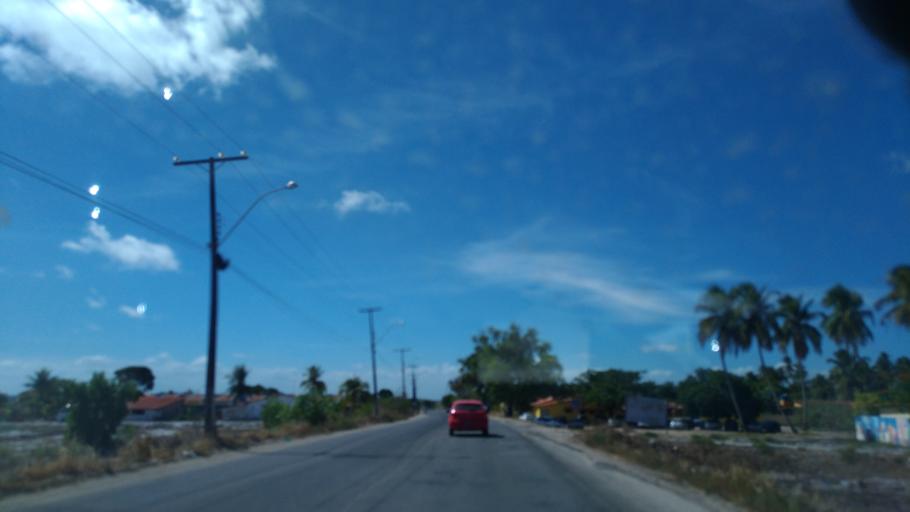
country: BR
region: Alagoas
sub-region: Marechal Deodoro
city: Marechal Deodoro
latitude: -9.7511
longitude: -35.8747
